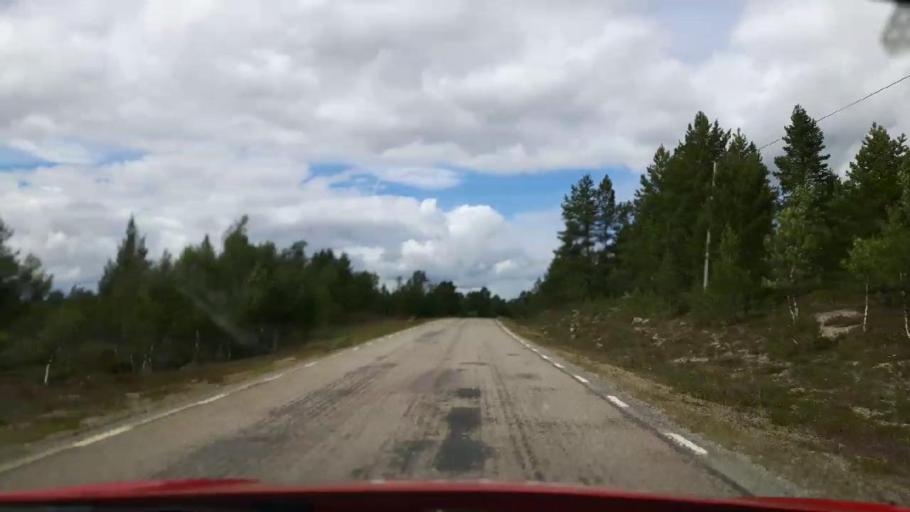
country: NO
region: Hedmark
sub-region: Engerdal
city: Engerdal
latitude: 62.2967
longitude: 12.8069
